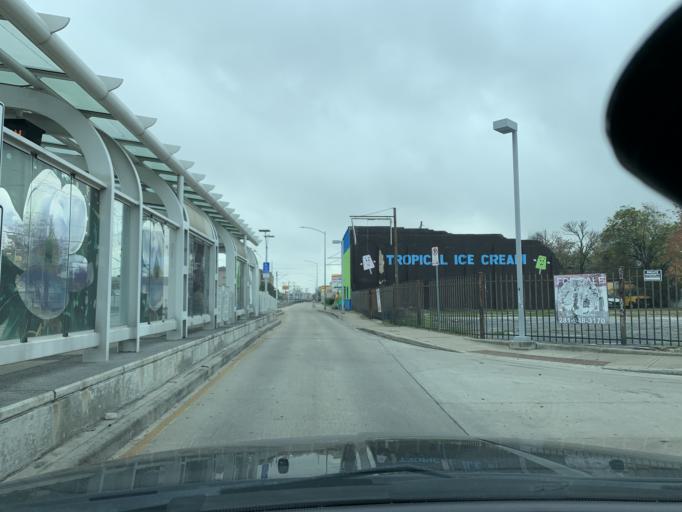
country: US
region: Texas
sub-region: Harris County
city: Houston
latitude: 29.7802
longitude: -95.3637
